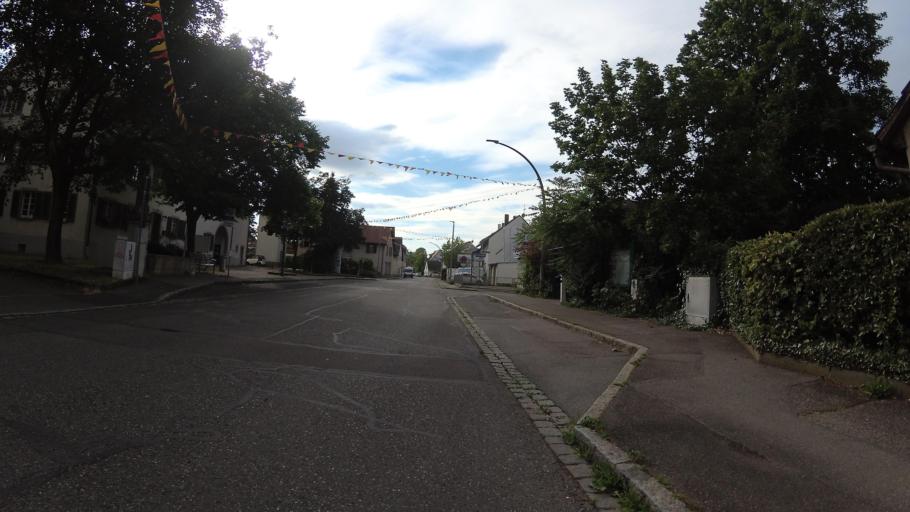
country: DE
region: Baden-Wuerttemberg
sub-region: Freiburg Region
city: Weil am Rhein
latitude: 47.5925
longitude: 7.6338
